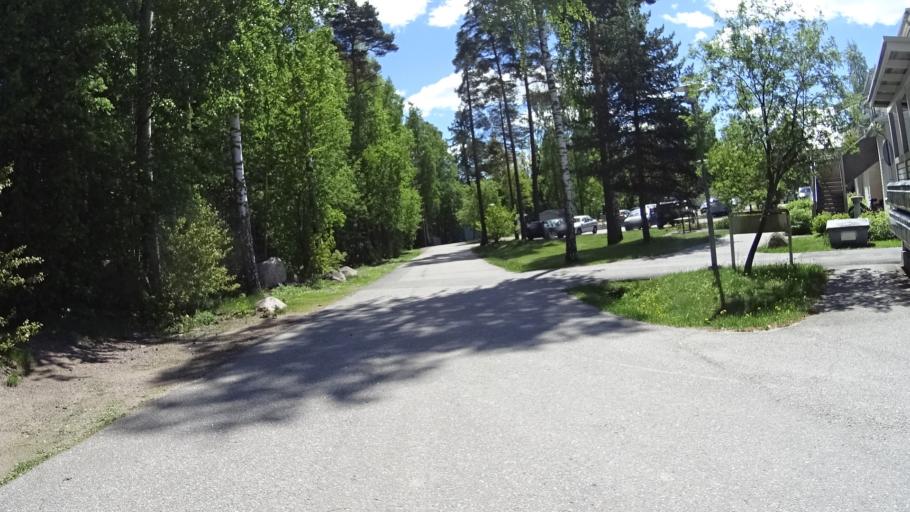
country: FI
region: Uusimaa
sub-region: Helsinki
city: Kauniainen
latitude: 60.2218
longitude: 24.6939
